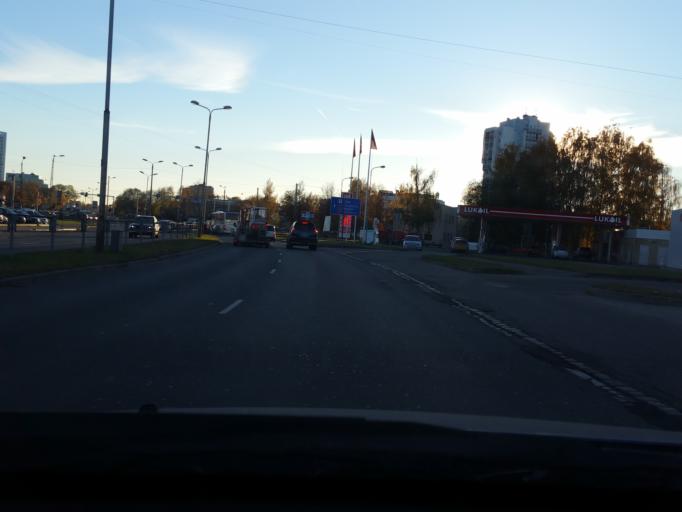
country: LV
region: Riga
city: Jaunciems
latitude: 56.9583
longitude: 24.1905
